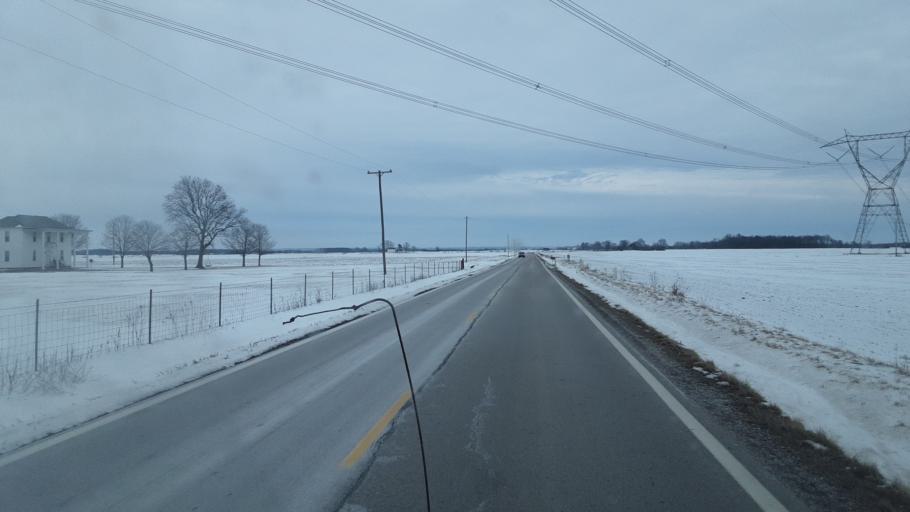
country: US
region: Ohio
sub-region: Pickaway County
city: Williamsport
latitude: 39.6396
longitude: -83.0877
